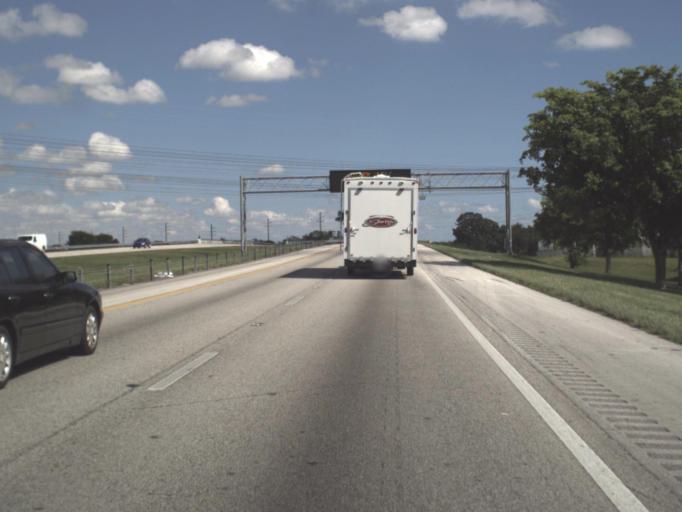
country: US
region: Florida
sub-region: Miami-Dade County
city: Princeton
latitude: 25.5238
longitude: -80.3994
